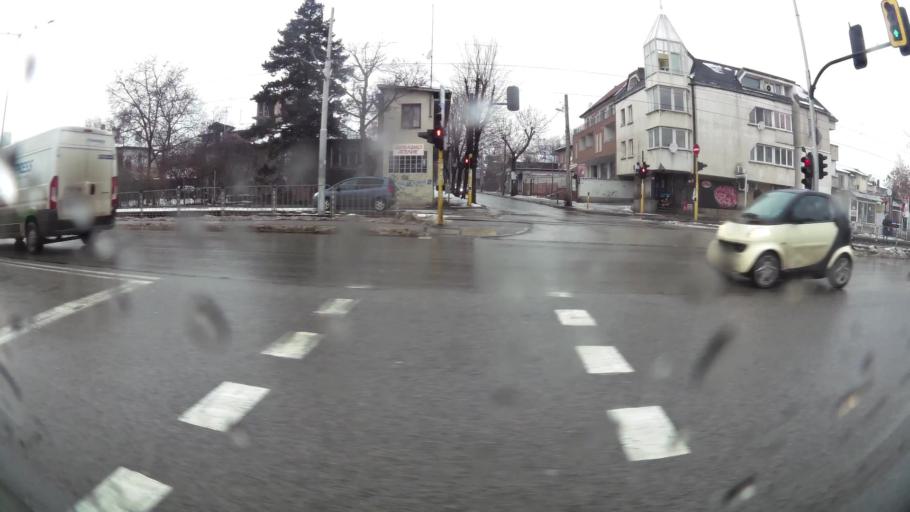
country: BG
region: Sofia-Capital
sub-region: Stolichna Obshtina
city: Sofia
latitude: 42.6802
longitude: 23.2692
